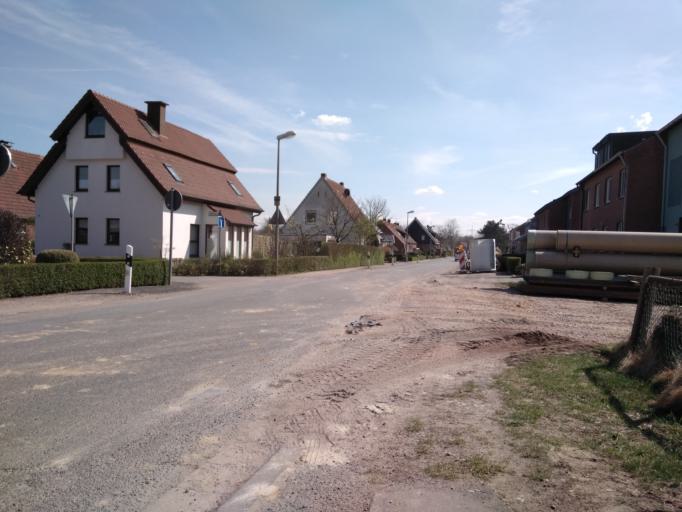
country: DE
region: North Rhine-Westphalia
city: Dorsten
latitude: 51.6521
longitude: 6.9255
